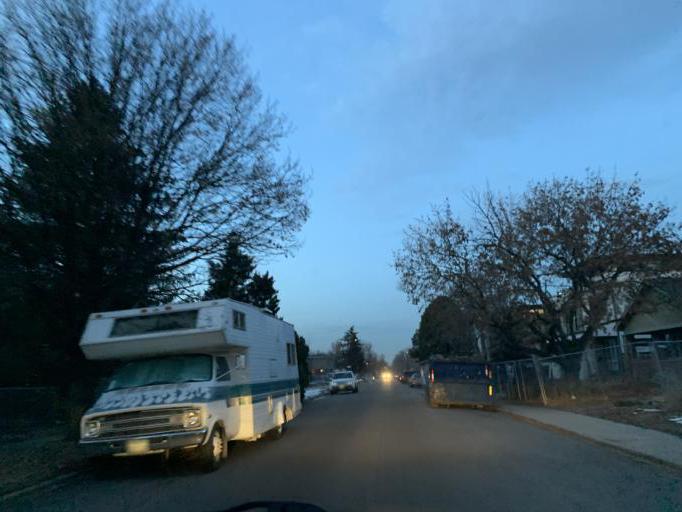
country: US
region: Colorado
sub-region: Jefferson County
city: Edgewater
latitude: 39.7741
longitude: -105.0393
